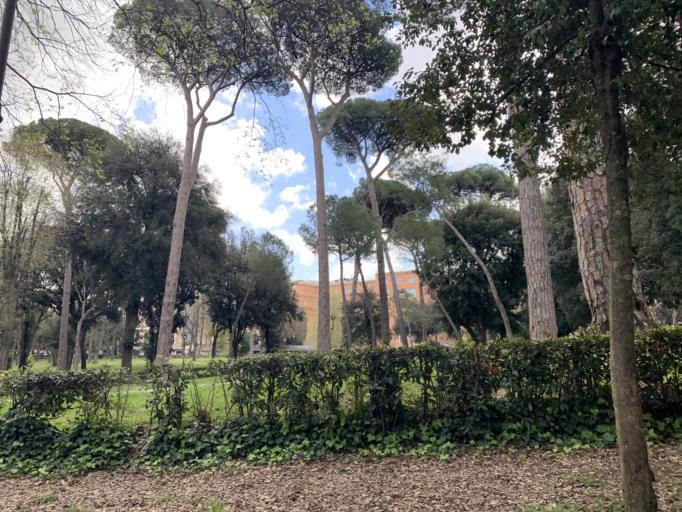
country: IT
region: Latium
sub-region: Citta metropolitana di Roma Capitale
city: Rome
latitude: 41.9122
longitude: 12.4901
